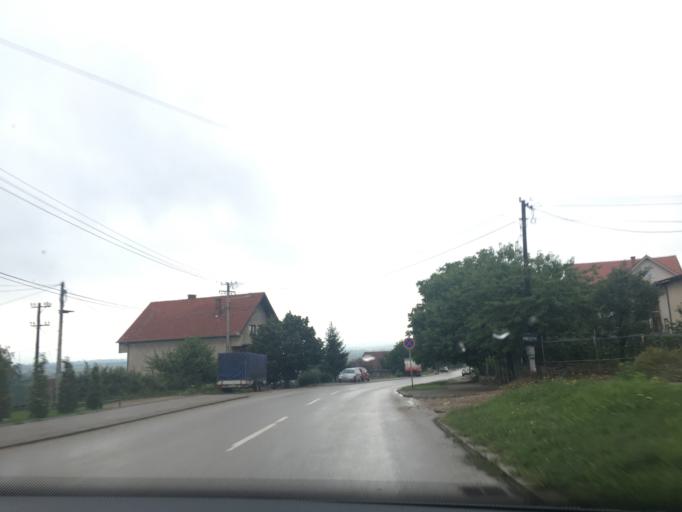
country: RS
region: Central Serbia
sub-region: Nisavski Okrug
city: Aleksinac
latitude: 43.5470
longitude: 21.6940
